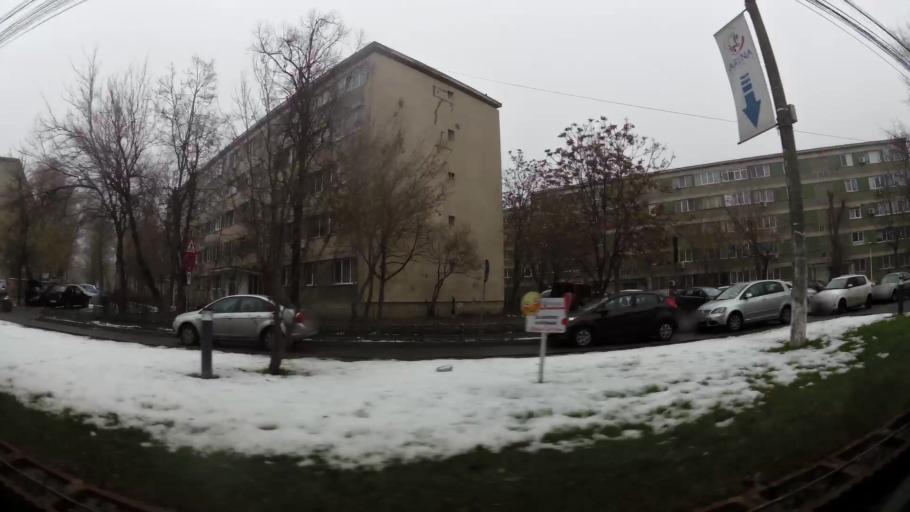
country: RO
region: Ilfov
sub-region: Comuna Chiajna
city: Rosu
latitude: 44.4571
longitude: 26.0421
